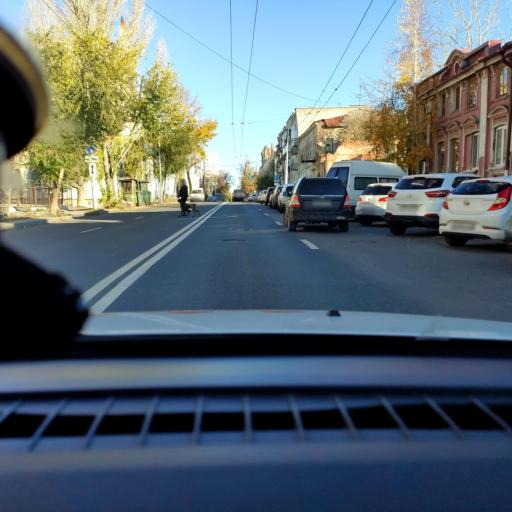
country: RU
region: Samara
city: Rozhdestveno
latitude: 53.1807
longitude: 50.0794
